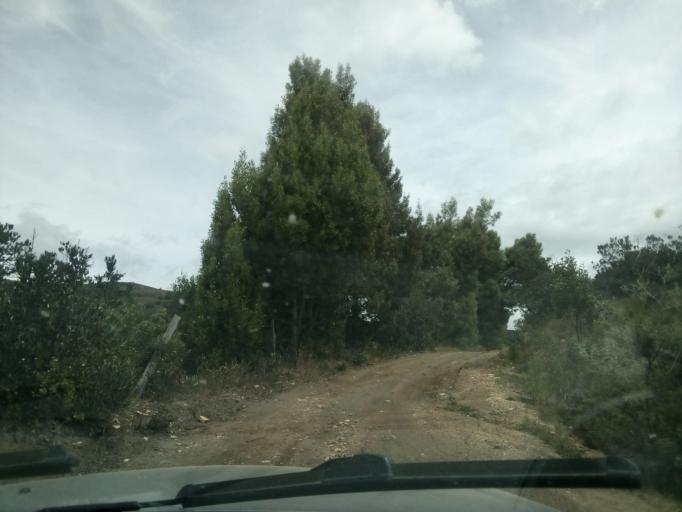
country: CO
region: Boyaca
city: Toca
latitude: 5.6042
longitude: -73.1125
